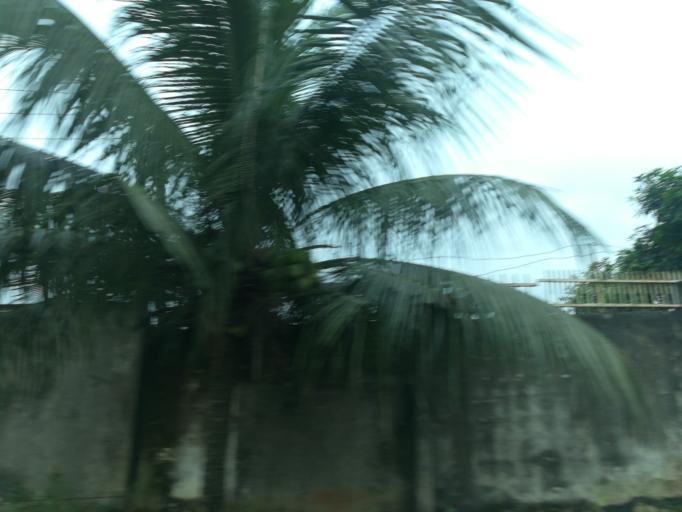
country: NG
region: Rivers
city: Port Harcourt
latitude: 4.8213
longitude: 7.0287
